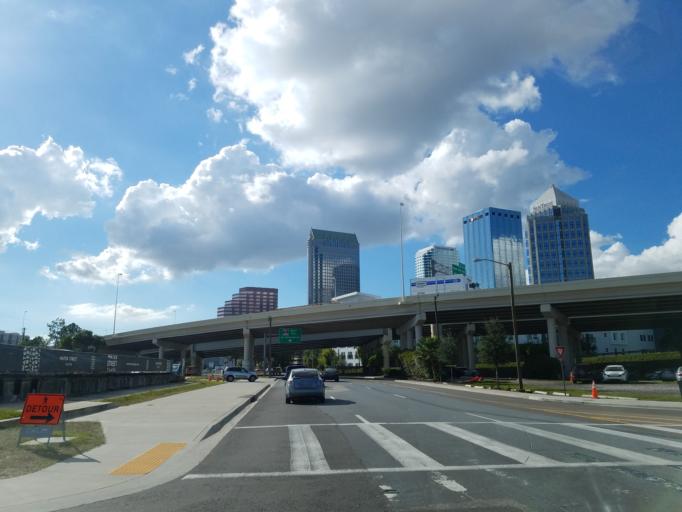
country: US
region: Florida
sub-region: Hillsborough County
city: Tampa
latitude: 27.9450
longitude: -82.4519
